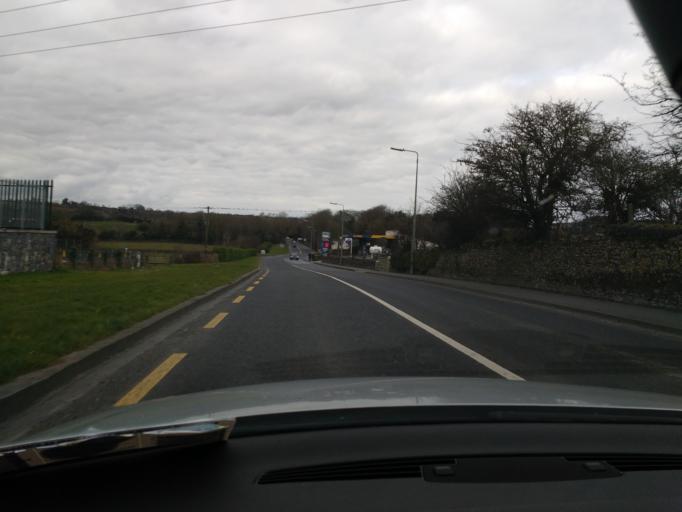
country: IE
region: Leinster
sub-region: Kilkenny
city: Kilkenny
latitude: 52.6731
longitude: -7.2692
